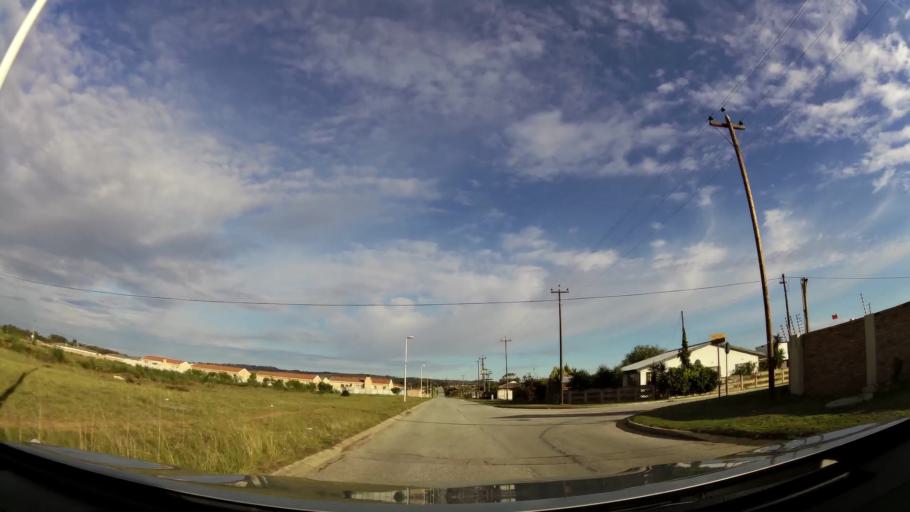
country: ZA
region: Eastern Cape
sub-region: Nelson Mandela Bay Metropolitan Municipality
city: Port Elizabeth
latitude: -33.9511
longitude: 25.4873
